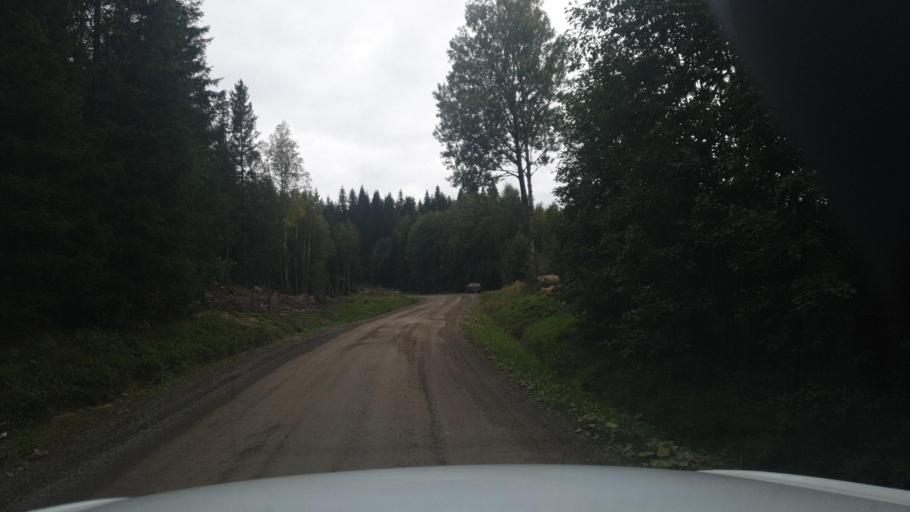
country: SE
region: Vaermland
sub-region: Sunne Kommun
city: Sunne
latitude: 59.8403
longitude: 12.9290
